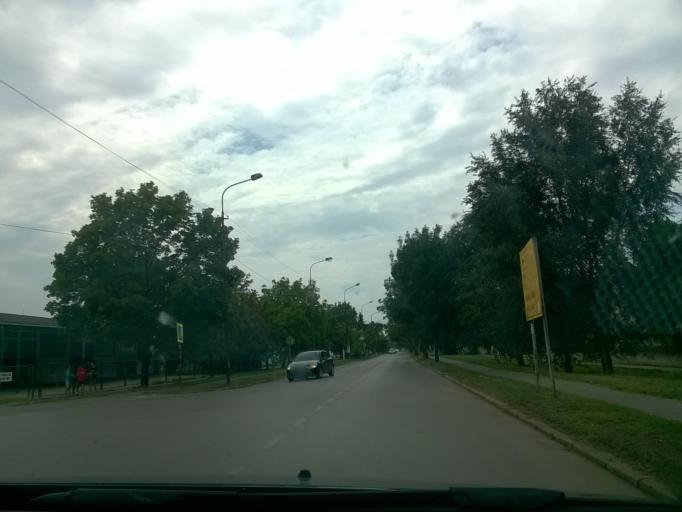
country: RS
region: Autonomna Pokrajina Vojvodina
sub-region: Srednjebanatski Okrug
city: Zrenjanin
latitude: 45.3958
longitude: 20.3925
